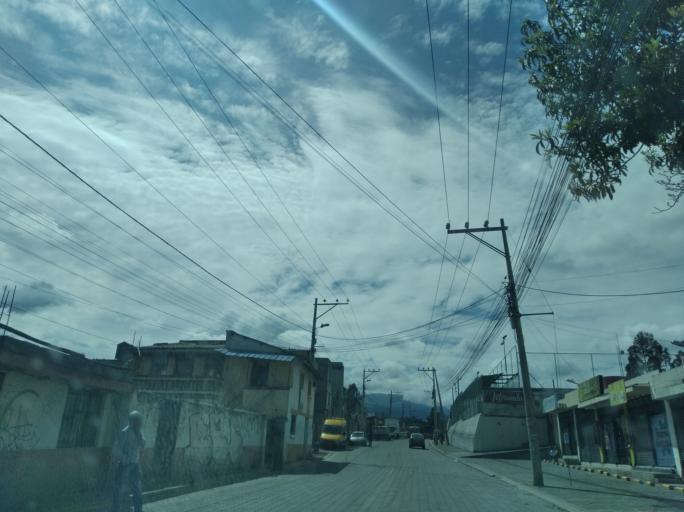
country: EC
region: Pichincha
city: Sangolqui
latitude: -0.2186
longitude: -78.3394
